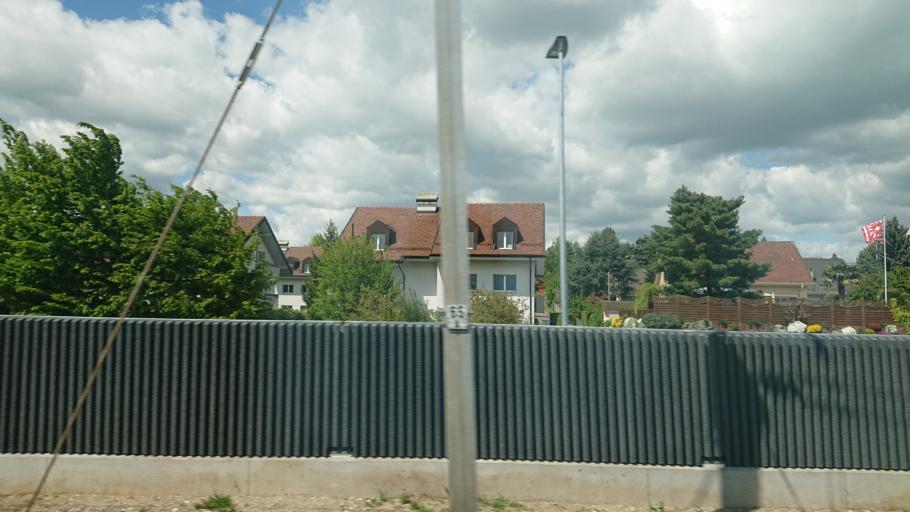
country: CH
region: Vaud
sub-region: Morges District
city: Saint-Prex
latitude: 46.4776
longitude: 6.4451
